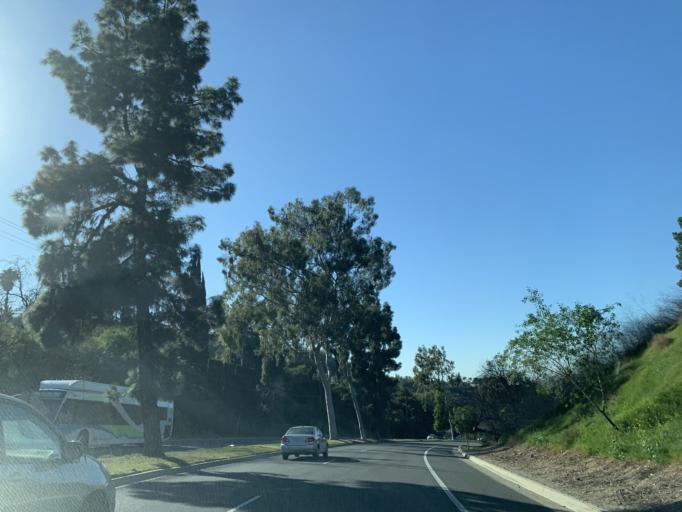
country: US
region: California
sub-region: Los Angeles County
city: Walnut
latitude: 34.0501
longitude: -117.8580
